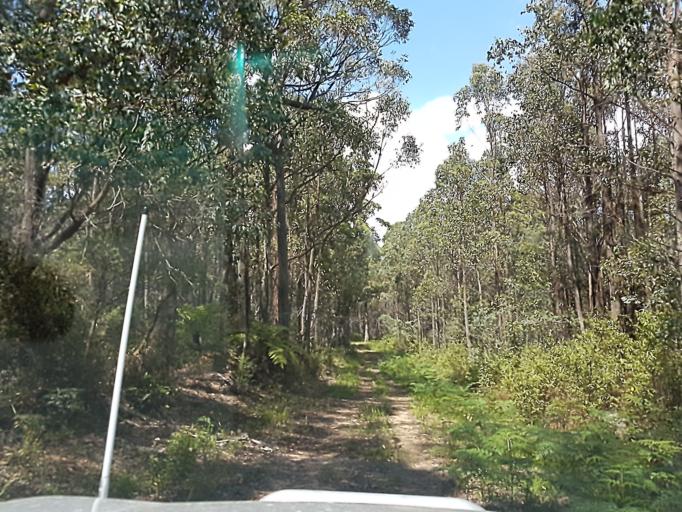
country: AU
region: Victoria
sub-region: East Gippsland
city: Lakes Entrance
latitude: -37.3179
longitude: 148.3287
